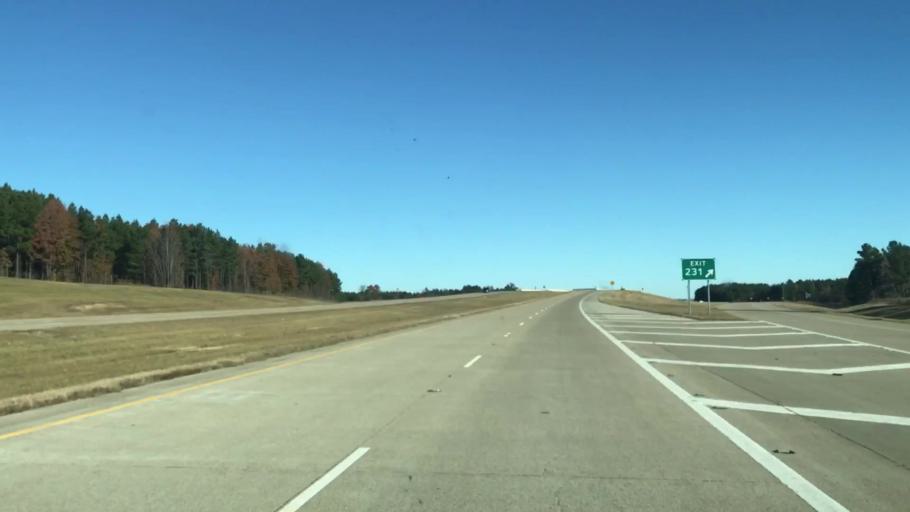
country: US
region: Louisiana
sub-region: Caddo Parish
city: Oil City
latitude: 32.8109
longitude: -93.8846
